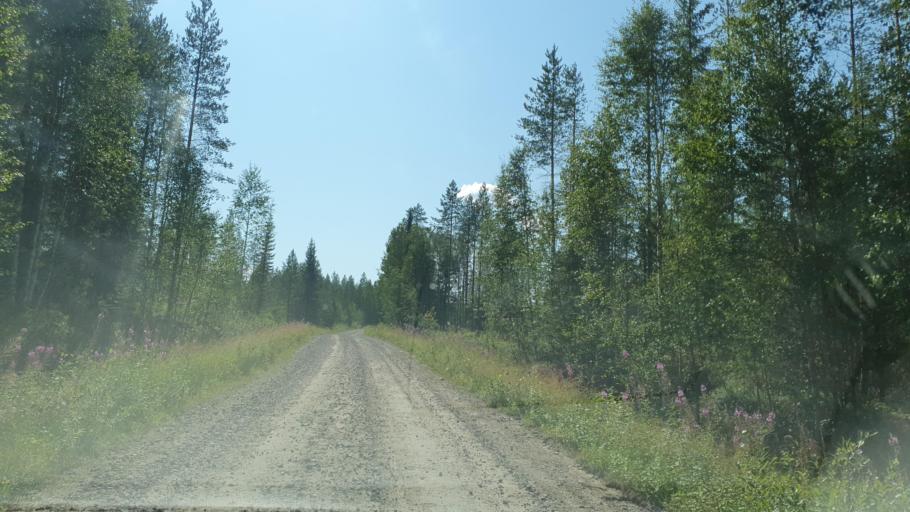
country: FI
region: Kainuu
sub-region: Kehys-Kainuu
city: Kuhmo
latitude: 64.0130
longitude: 29.5944
